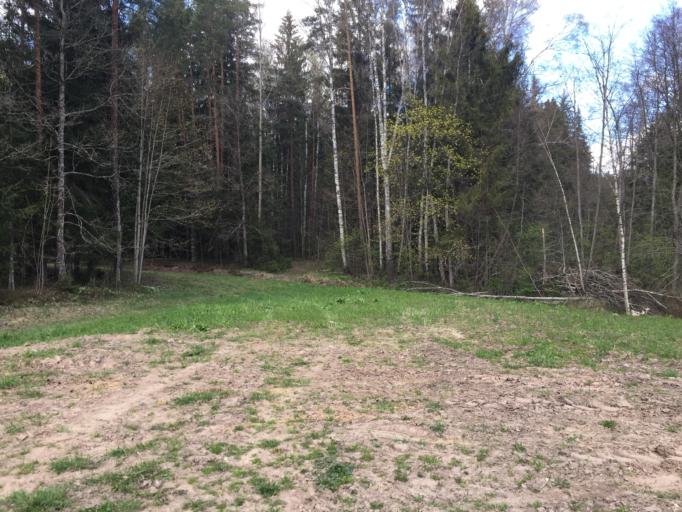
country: LV
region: Baldone
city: Baldone
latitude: 56.7473
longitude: 24.3830
